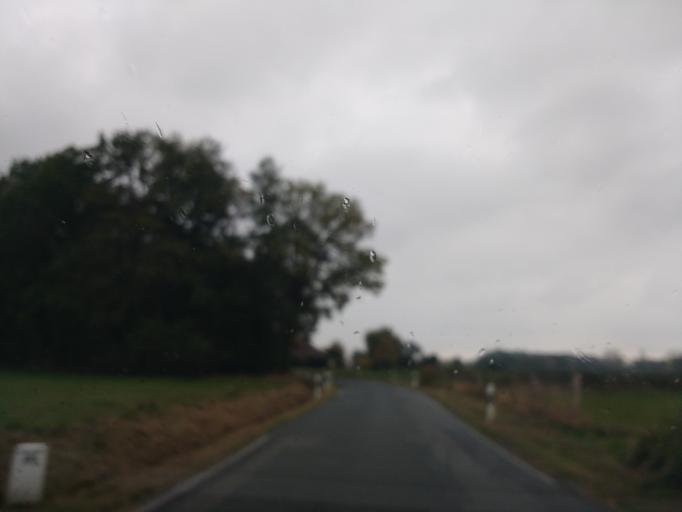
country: DE
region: North Rhine-Westphalia
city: Borgholzhausen
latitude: 52.0577
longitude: 8.2966
